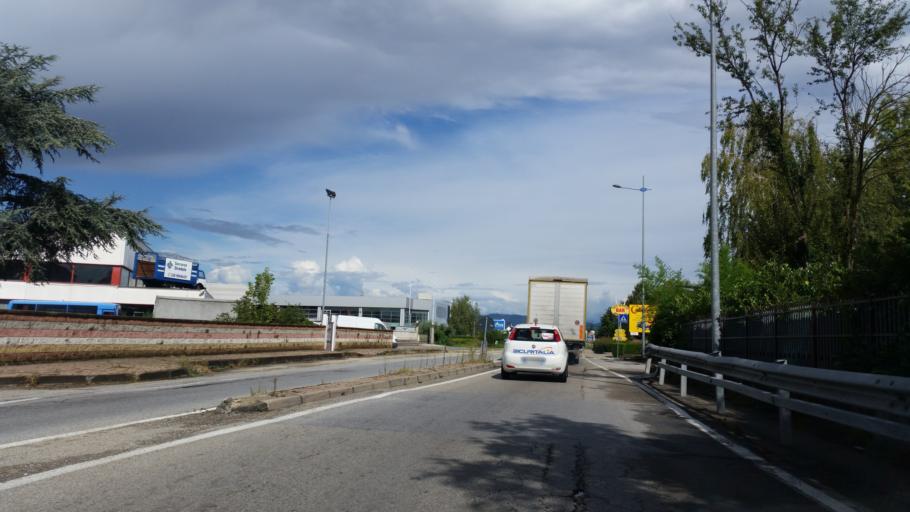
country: IT
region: Piedmont
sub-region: Provincia di Torino
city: Poirino
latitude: 44.9283
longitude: 7.8351
